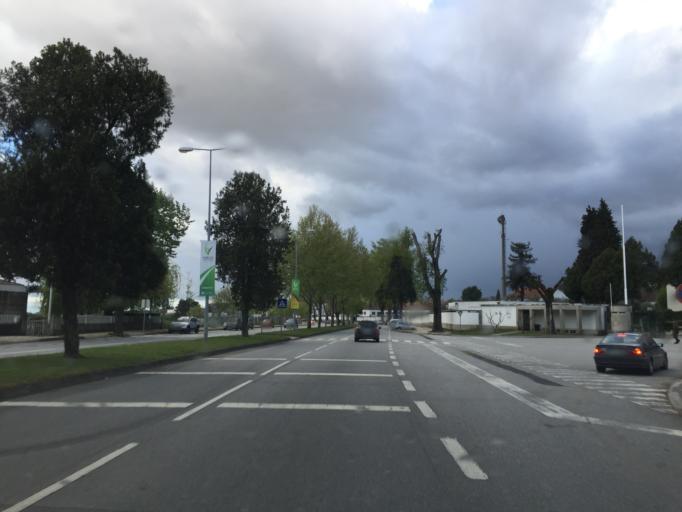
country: PT
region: Viseu
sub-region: Viseu
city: Viseu
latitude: 40.6472
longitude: -7.9214
